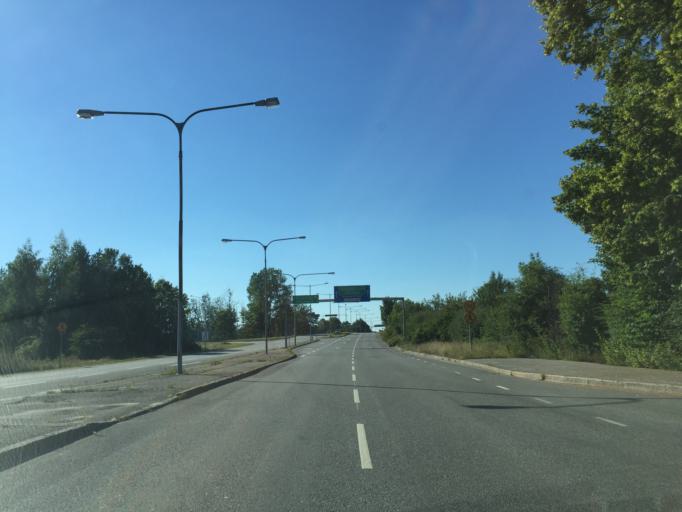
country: SE
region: OErebro
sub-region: Orebro Kommun
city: Orebro
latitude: 59.2757
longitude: 15.1840
